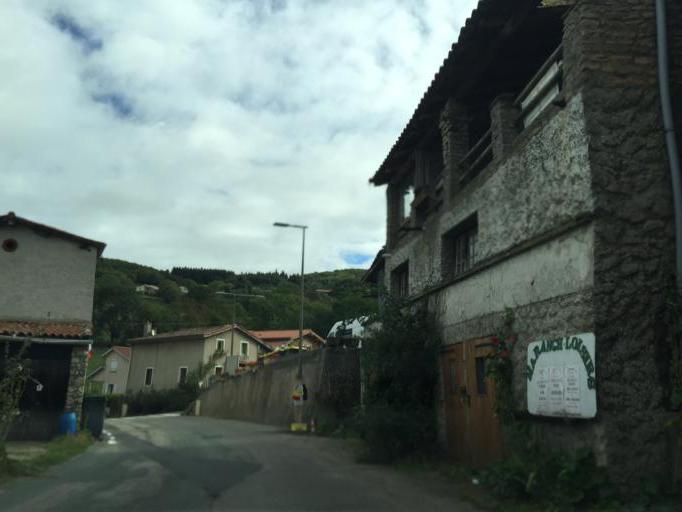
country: FR
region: Rhone-Alpes
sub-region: Departement de la Loire
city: Pelussin
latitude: 45.4653
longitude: 4.6706
